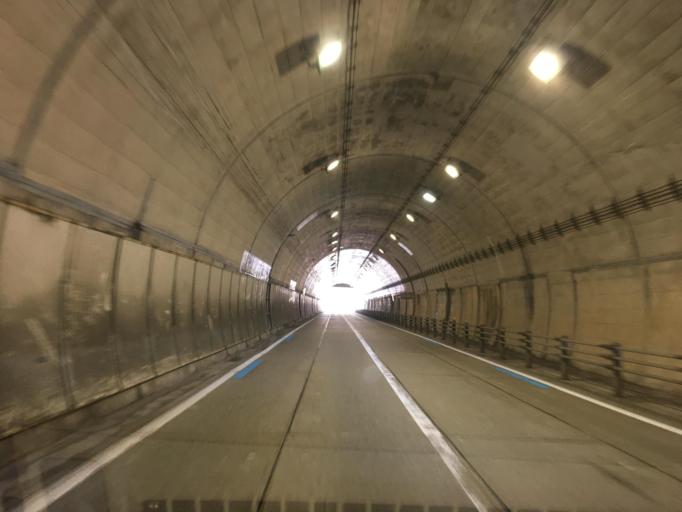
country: JP
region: Toyama
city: Himi
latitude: 36.8909
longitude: 137.0032
